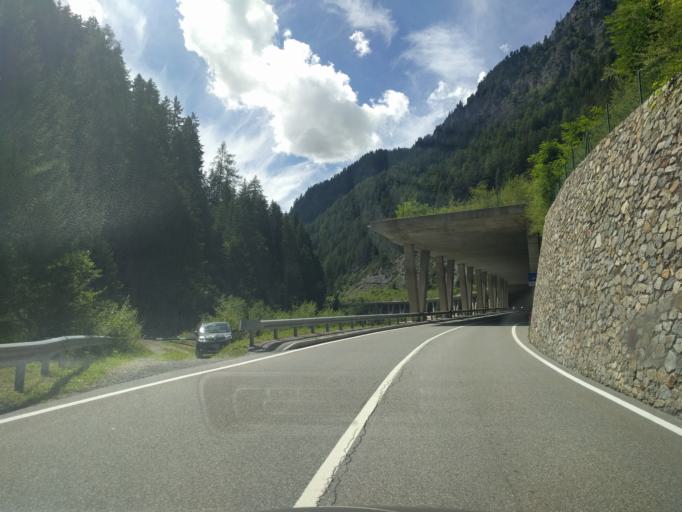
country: IT
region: Trentino-Alto Adige
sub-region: Bolzano
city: Stelvio
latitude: 46.5698
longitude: 10.5270
